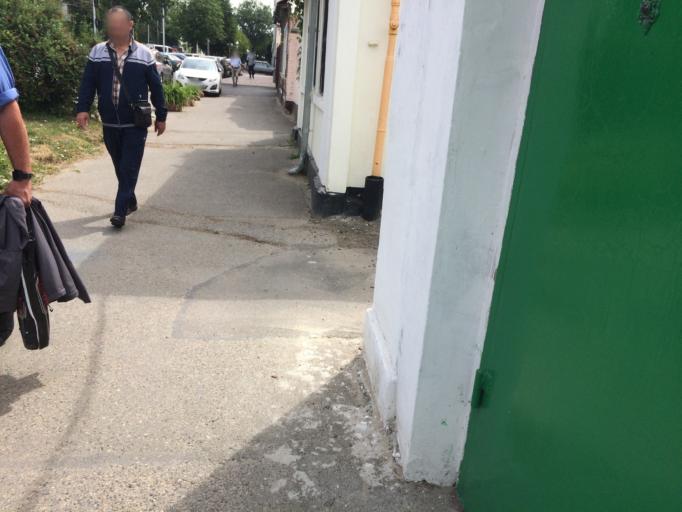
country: RU
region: Stavropol'skiy
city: Stavropol'
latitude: 45.0432
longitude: 41.9591
